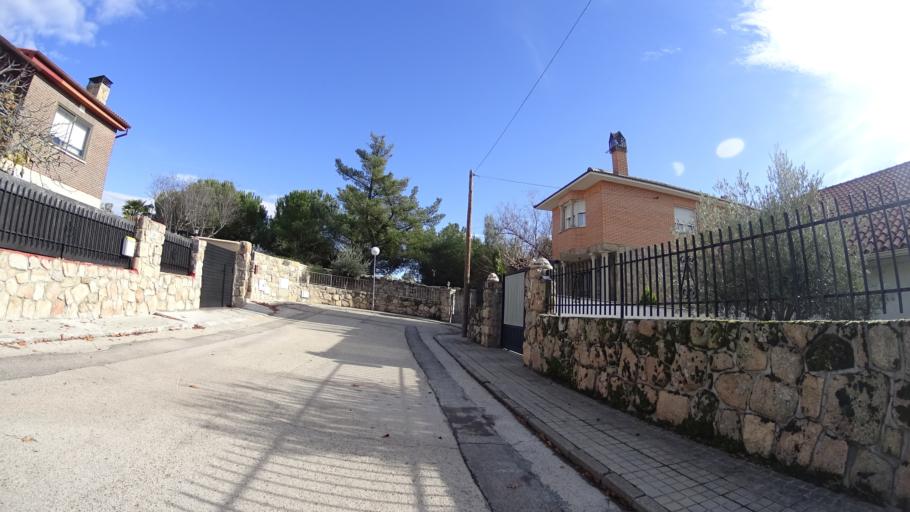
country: ES
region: Madrid
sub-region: Provincia de Madrid
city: Galapagar
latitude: 40.5794
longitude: -4.0180
